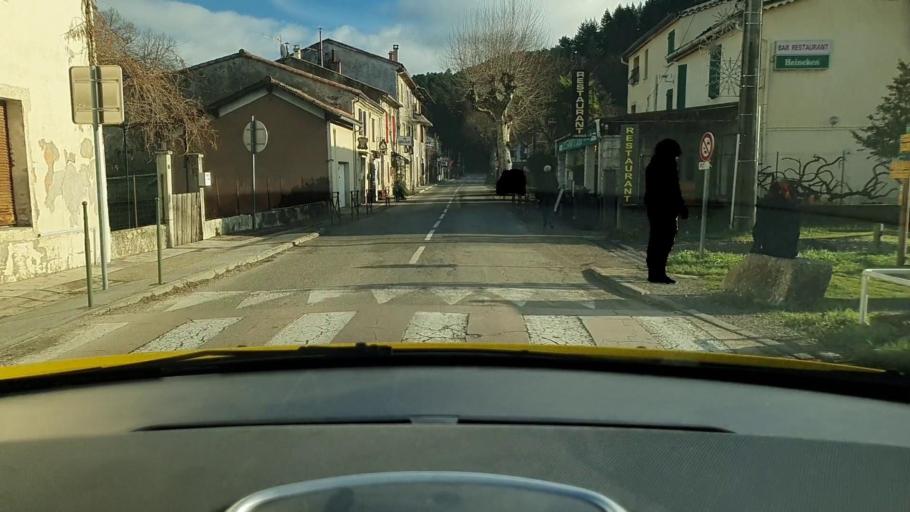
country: FR
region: Languedoc-Roussillon
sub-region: Departement du Gard
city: Branoux-les-Taillades
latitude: 44.3044
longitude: 3.9733
